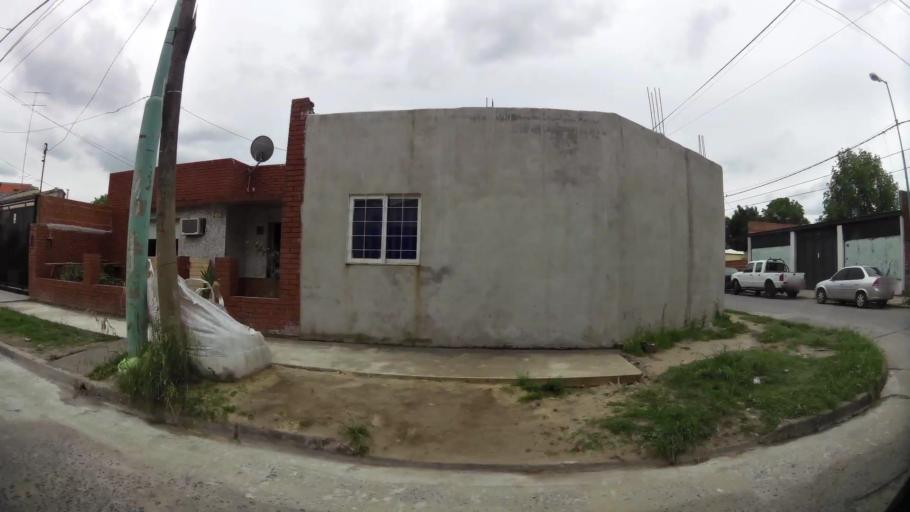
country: AR
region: Buenos Aires
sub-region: Partido de Zarate
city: Zarate
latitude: -34.1076
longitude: -59.0130
